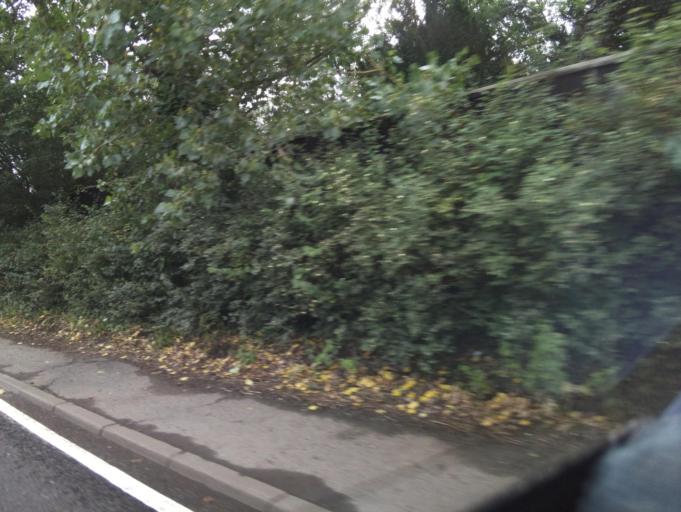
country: GB
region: England
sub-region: Nottinghamshire
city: Burton Joyce
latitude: 52.9835
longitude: -1.0444
